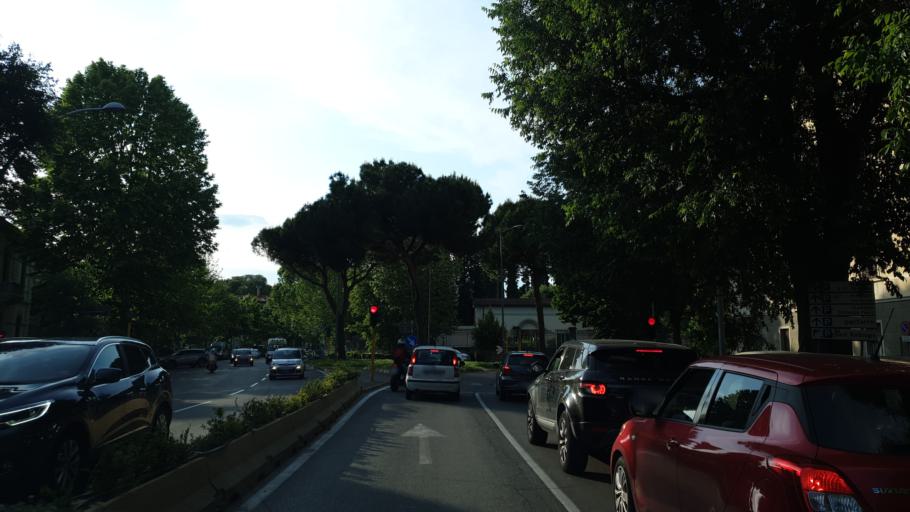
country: IT
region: Tuscany
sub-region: Province of Florence
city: Florence
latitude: 43.7763
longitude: 11.2691
